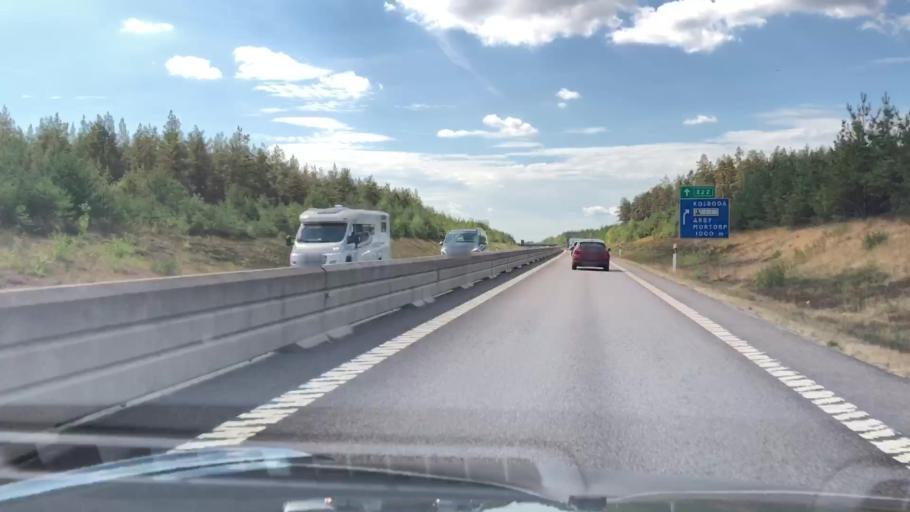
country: SE
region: Kalmar
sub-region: Kalmar Kommun
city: Ljungbyholm
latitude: 56.6002
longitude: 16.1297
